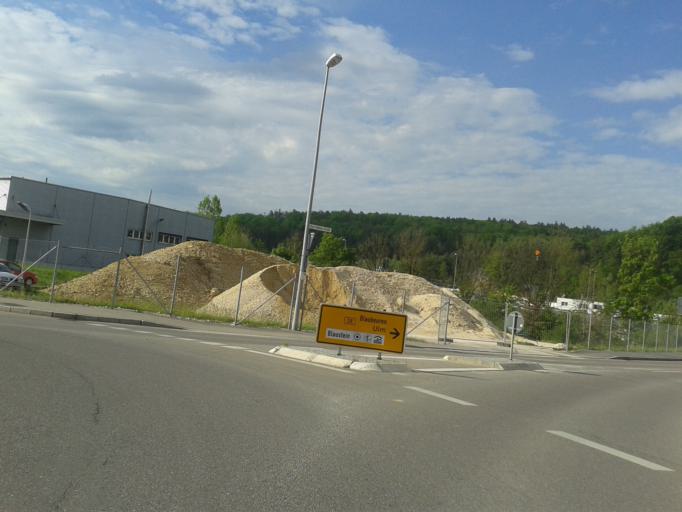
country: DE
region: Baden-Wuerttemberg
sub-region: Tuebingen Region
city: Dornstadt
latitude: 48.4143
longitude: 9.9231
